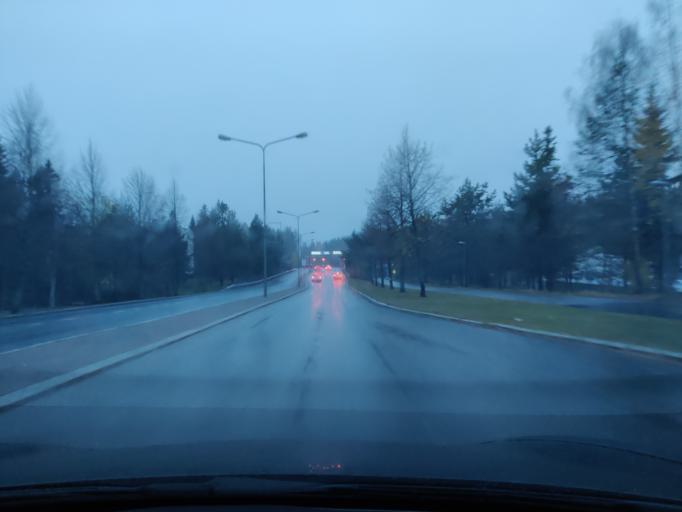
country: FI
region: Northern Savo
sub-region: Kuopio
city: Kuopio
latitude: 62.8365
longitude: 27.6584
